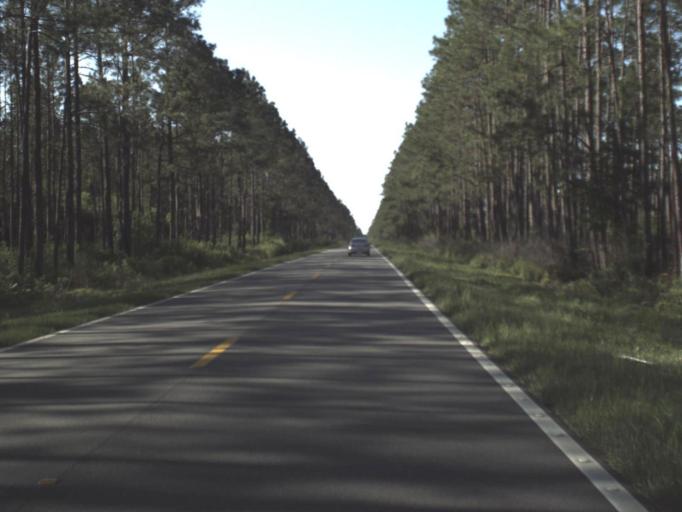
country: US
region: Florida
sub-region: Gulf County
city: Wewahitchka
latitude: 30.0930
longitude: -84.9845
